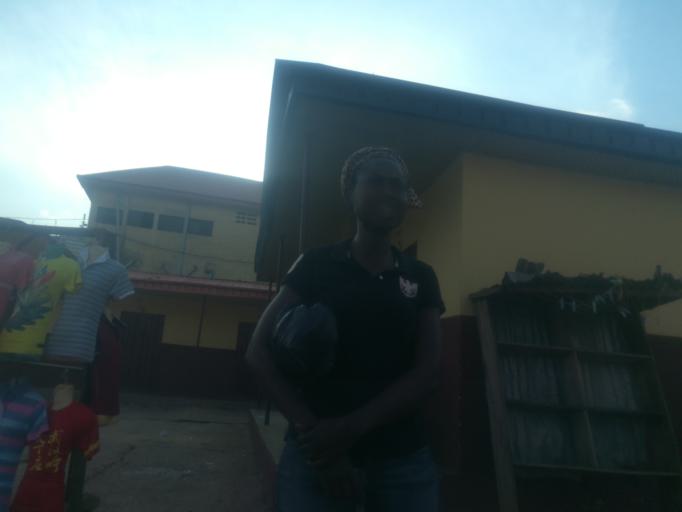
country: NG
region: Oyo
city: Ibadan
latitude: 7.3904
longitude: 3.8817
